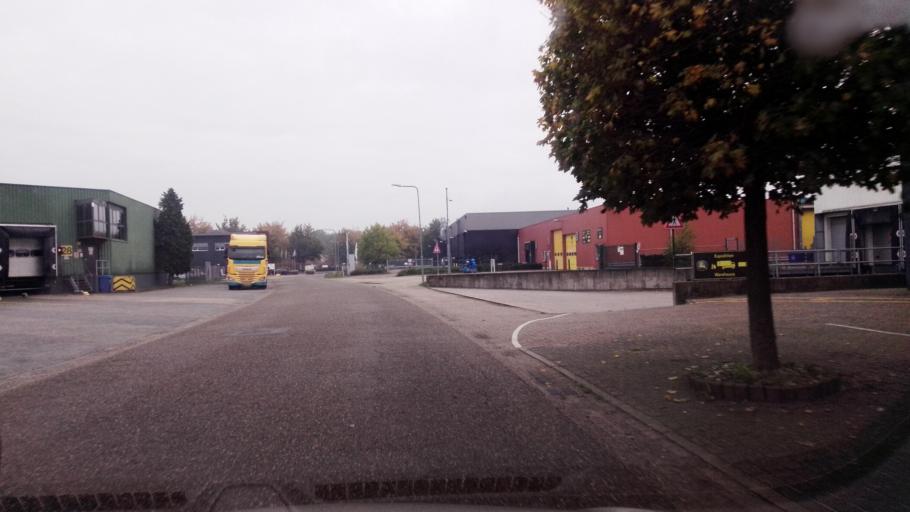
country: NL
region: Limburg
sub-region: Gemeente Peel en Maas
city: Maasbree
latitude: 51.4438
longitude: 6.0549
